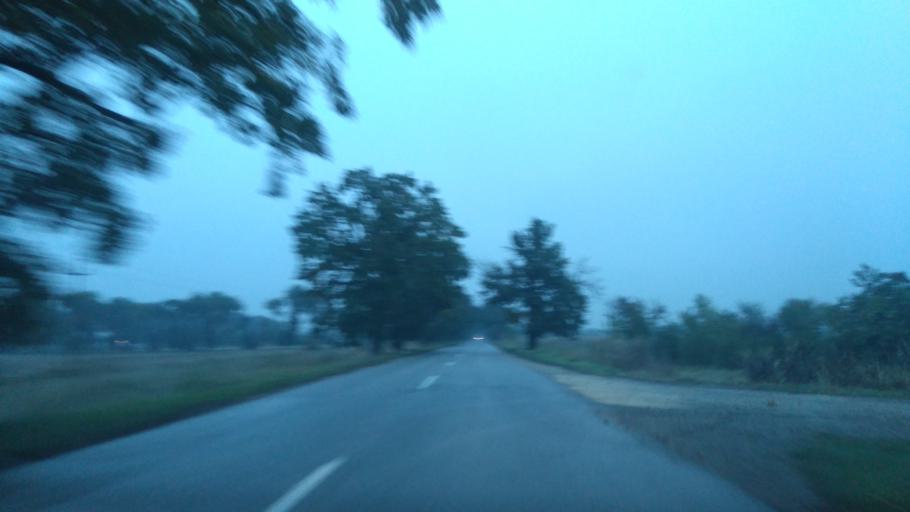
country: RS
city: Backo Petrovo Selo
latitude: 45.6878
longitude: 20.0751
